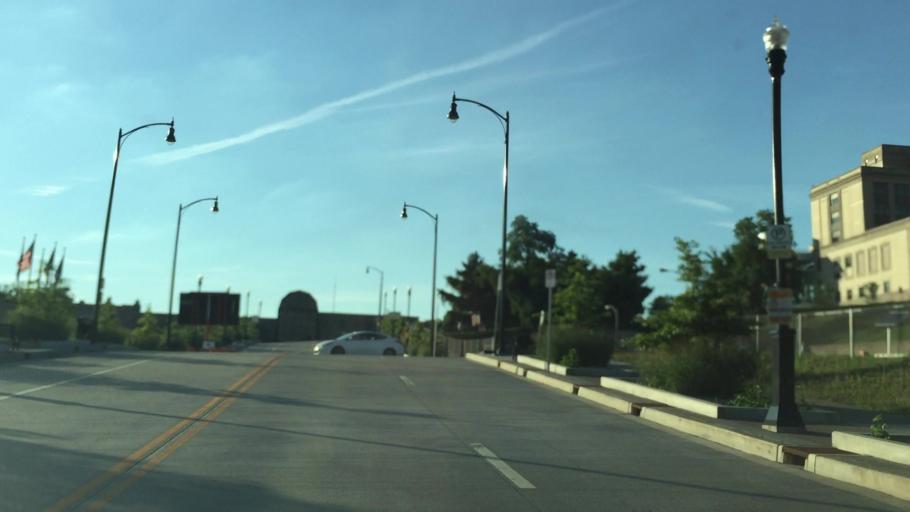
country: US
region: Pennsylvania
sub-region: Allegheny County
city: Pittsburgh
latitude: 40.4420
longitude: -79.9892
